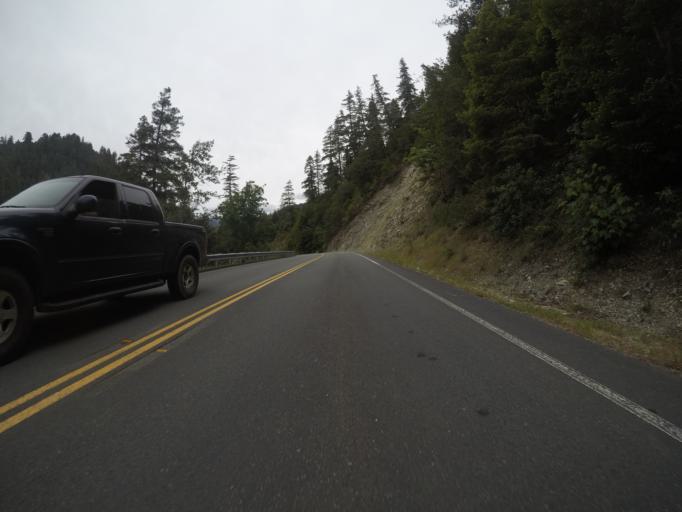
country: US
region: California
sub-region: Del Norte County
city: Bertsch-Oceanview
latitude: 41.7153
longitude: -123.9443
